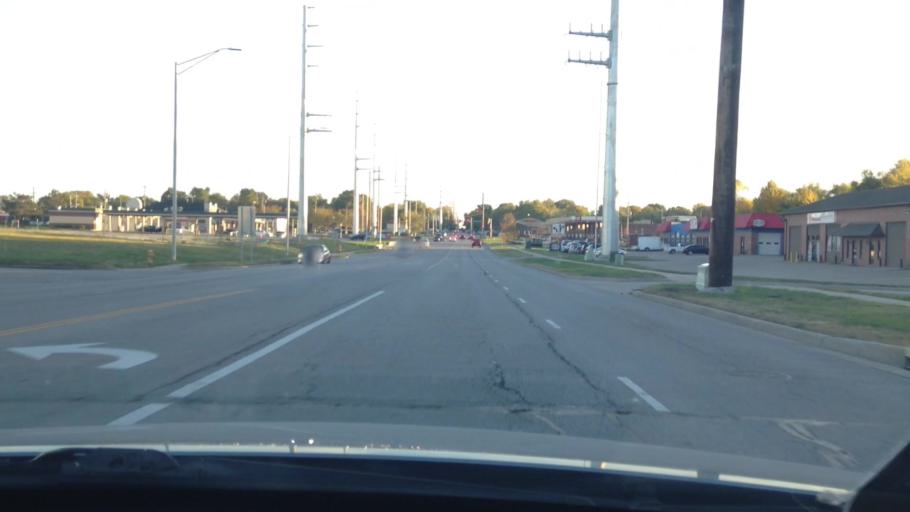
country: US
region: Kansas
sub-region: Johnson County
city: Olathe
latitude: 38.8866
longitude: -94.7973
